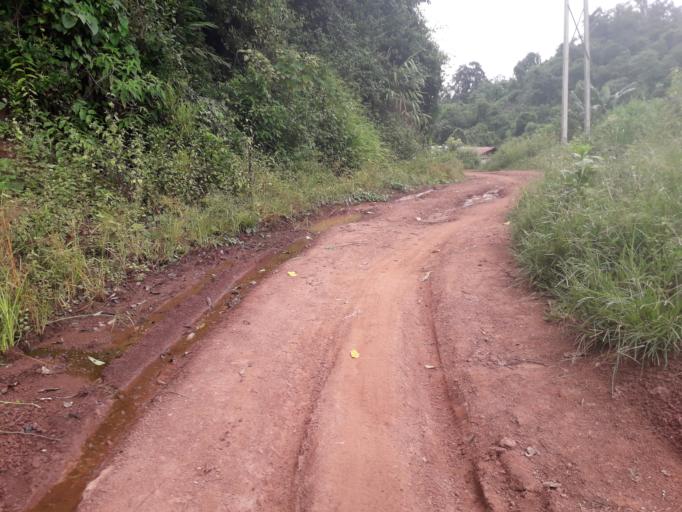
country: CN
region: Yunnan
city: Menglie
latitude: 22.2166
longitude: 101.6540
